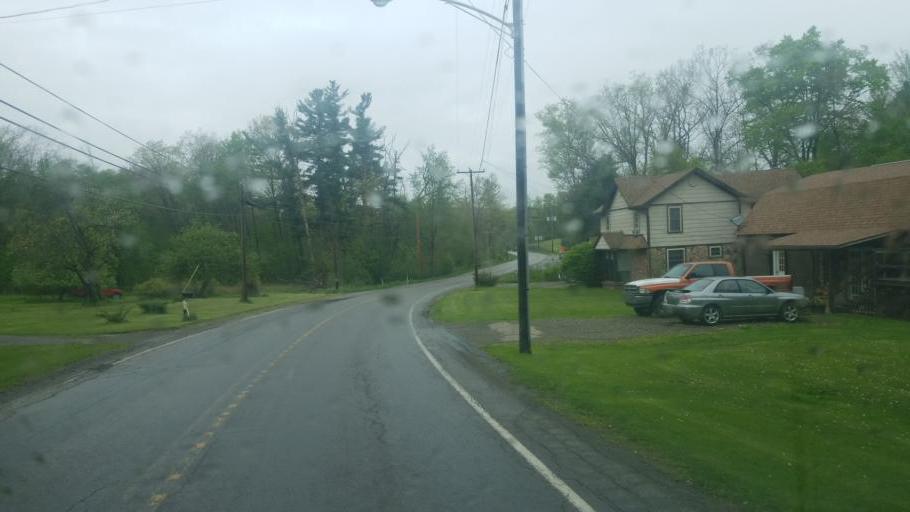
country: US
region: Pennsylvania
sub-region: Clarion County
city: Marianne
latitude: 41.3763
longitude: -79.3115
